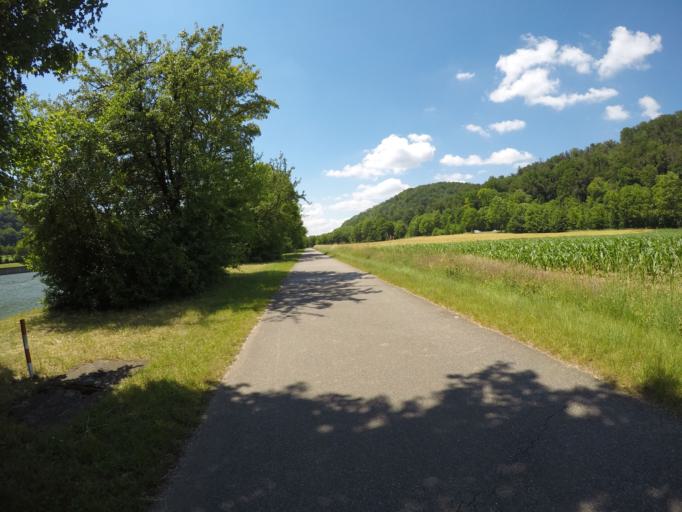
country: DE
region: Bavaria
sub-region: Lower Bavaria
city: Ihrlerstein
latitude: 48.9250
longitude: 11.8452
